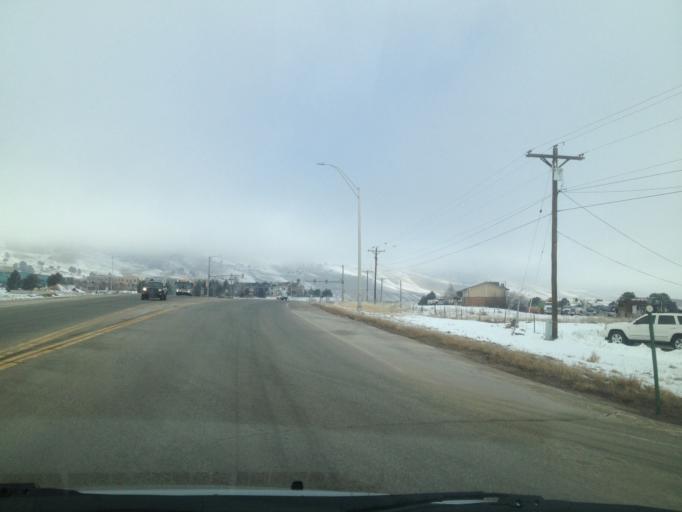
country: US
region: Colorado
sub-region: Boulder County
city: Boulder
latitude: 40.0638
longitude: -105.2797
